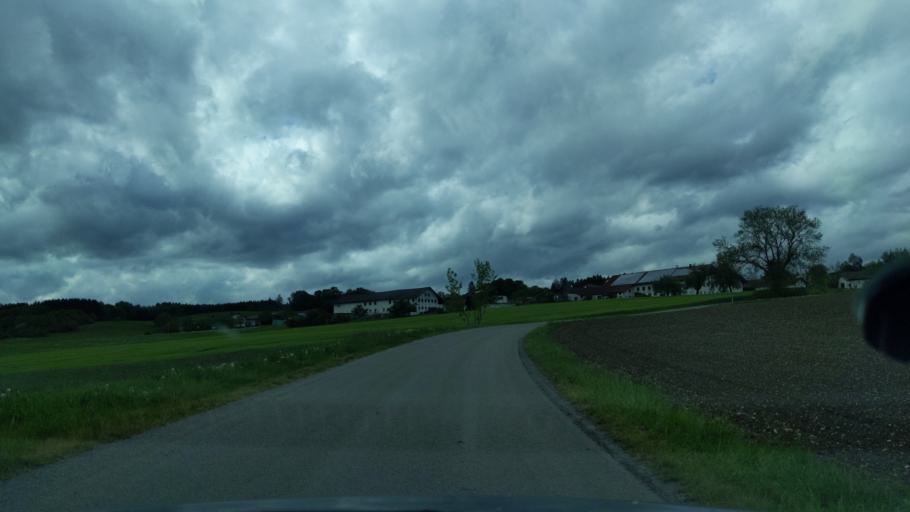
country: DE
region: Bavaria
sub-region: Upper Bavaria
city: Steinhoring
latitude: 48.1132
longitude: 12.0110
